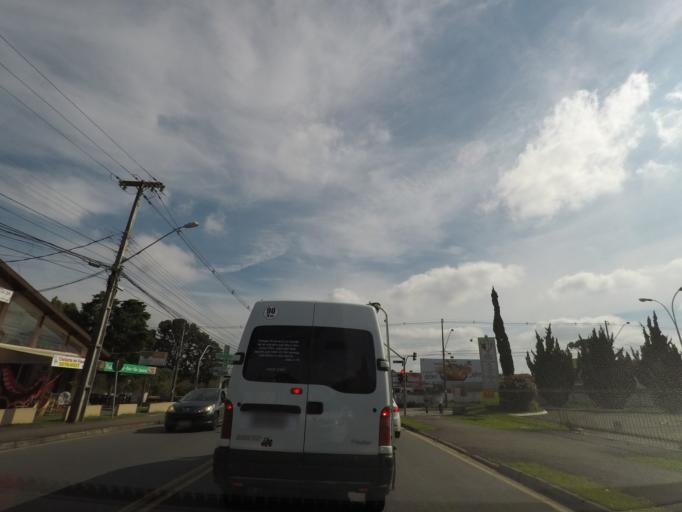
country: BR
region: Parana
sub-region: Sao Jose Dos Pinhais
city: Sao Jose dos Pinhais
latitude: -25.5096
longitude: -49.2531
